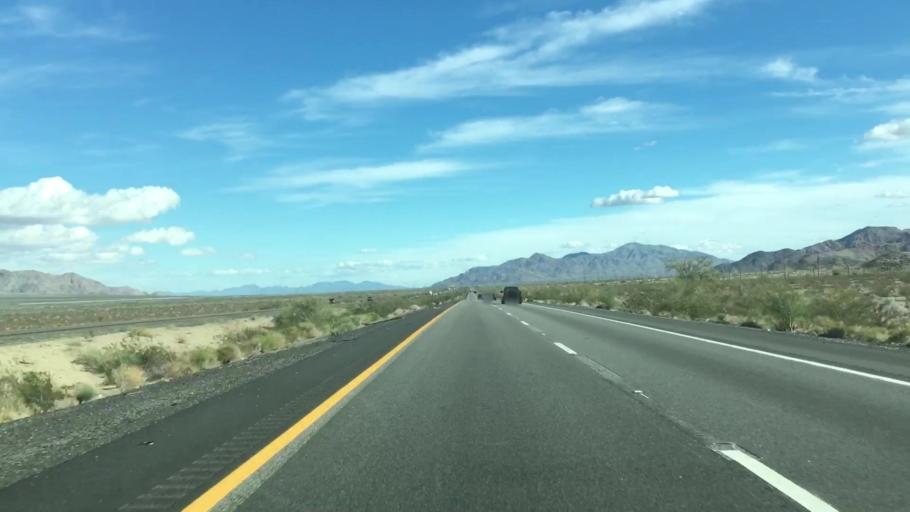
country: US
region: California
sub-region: Imperial County
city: Niland
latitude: 33.6693
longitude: -115.6380
